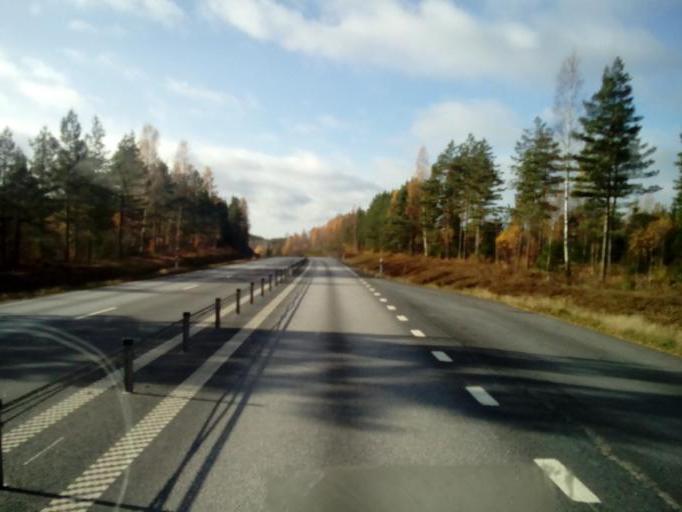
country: SE
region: Kalmar
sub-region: Vimmerby Kommun
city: Vimmerby
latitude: 57.6774
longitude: 15.9424
